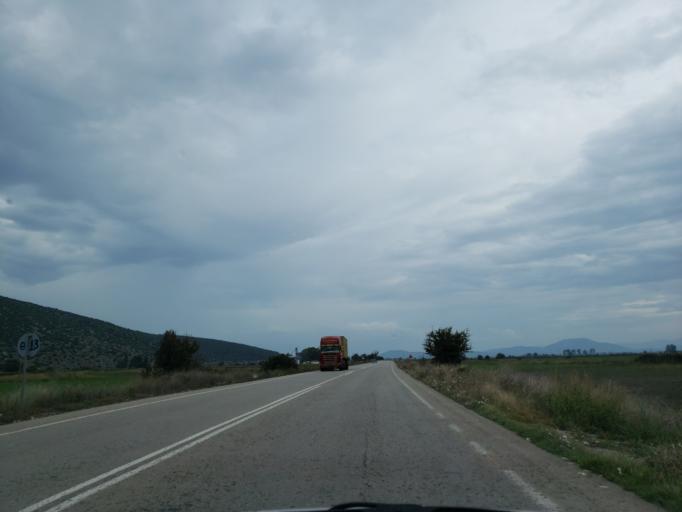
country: GR
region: Central Greece
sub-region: Nomos Voiotias
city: Orchomenos
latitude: 38.4887
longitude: 23.0652
